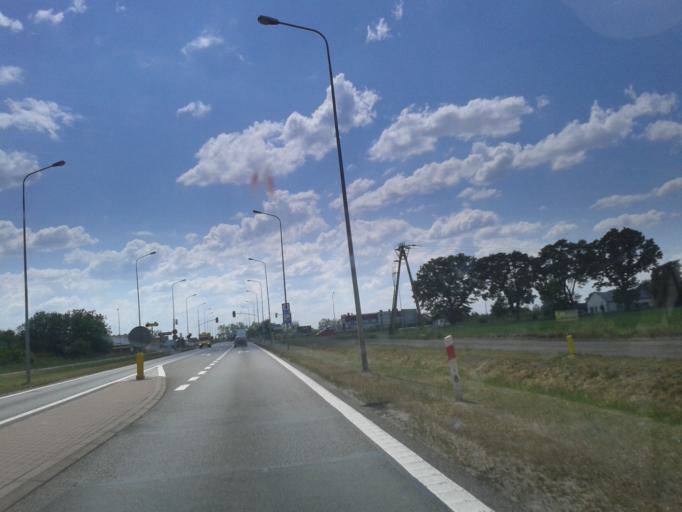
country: PL
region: Pomeranian Voivodeship
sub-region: Powiat czluchowski
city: Czluchow
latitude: 53.6654
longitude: 17.3474
